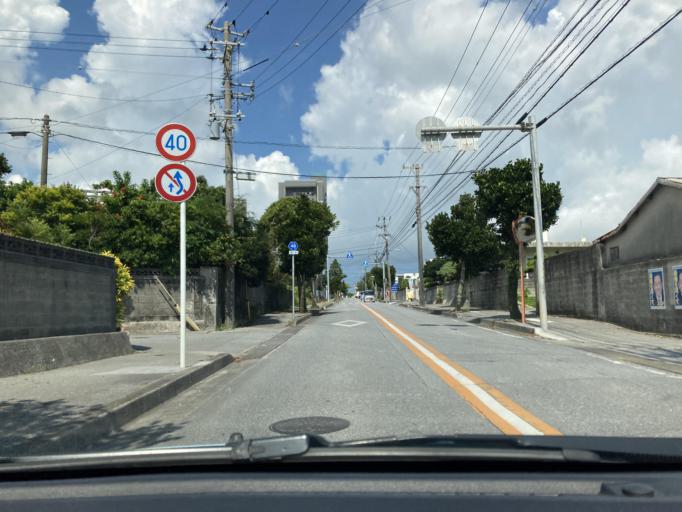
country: JP
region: Okinawa
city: Tomigusuku
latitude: 26.1584
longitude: 127.7474
